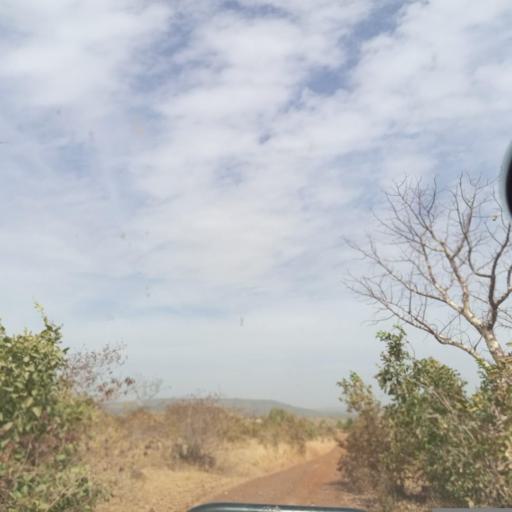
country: ML
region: Koulikoro
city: Koulikoro
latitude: 13.1618
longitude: -7.7272
